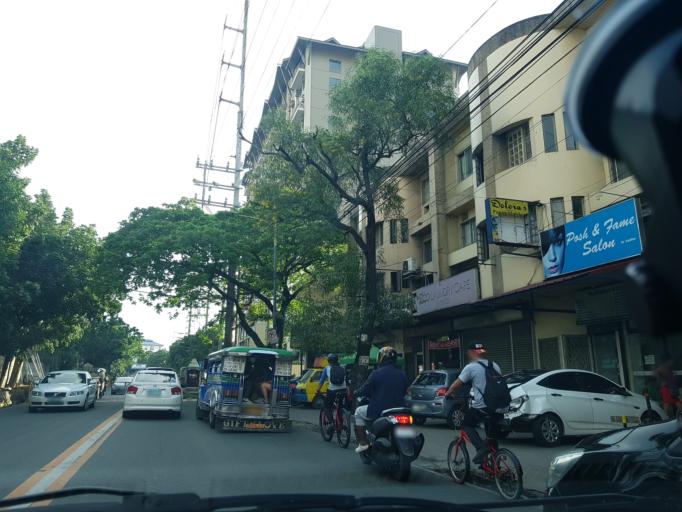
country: PH
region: Metro Manila
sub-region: Marikina
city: Calumpang
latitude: 14.6061
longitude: 121.0922
